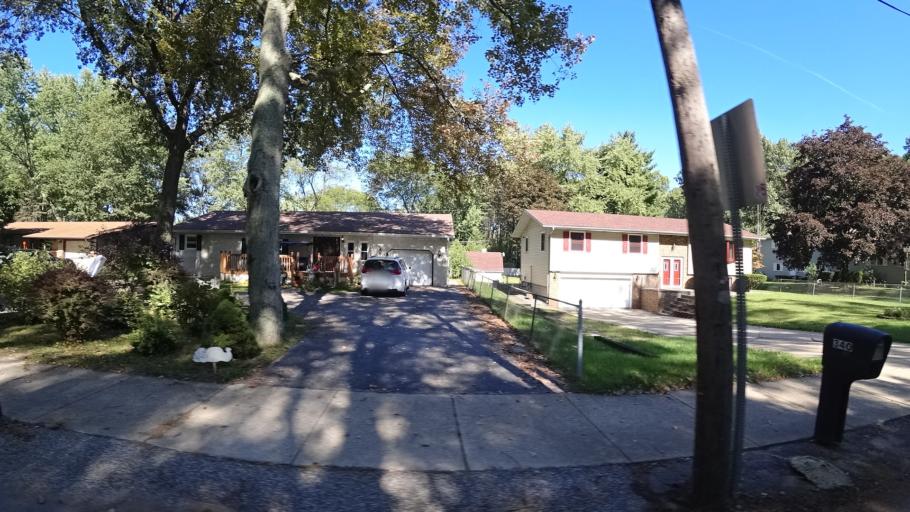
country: US
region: Indiana
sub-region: LaPorte County
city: Michigan City
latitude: 41.6875
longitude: -86.8849
